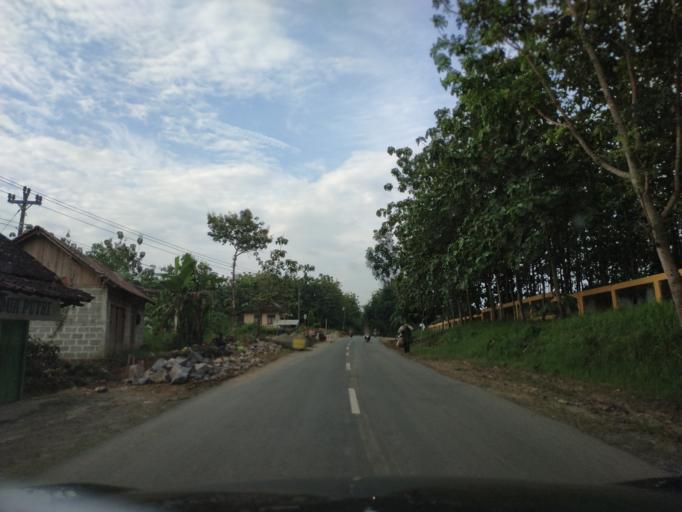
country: ID
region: Central Java
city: Medang
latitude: -6.9050
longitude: 111.4420
